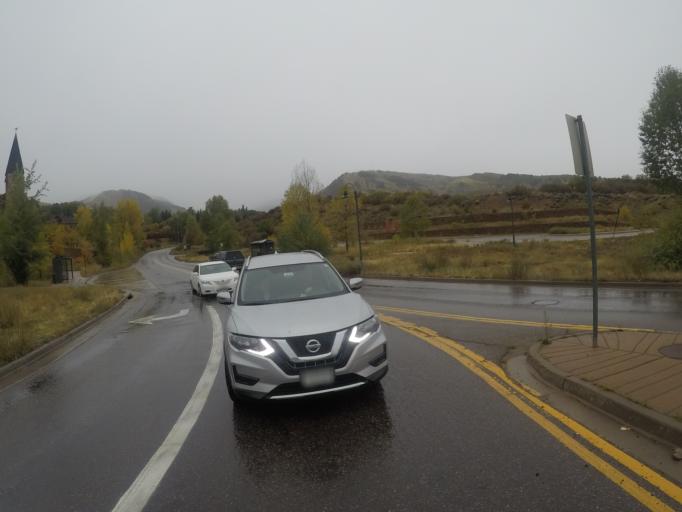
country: US
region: Colorado
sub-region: Pitkin County
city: Aspen
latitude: 39.1953
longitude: -106.8406
